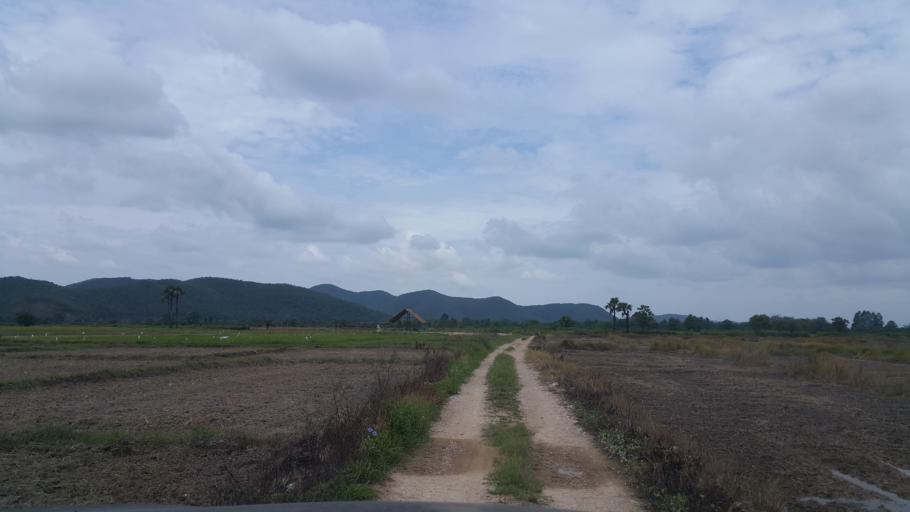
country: TH
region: Lamphun
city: Ban Thi
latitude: 18.6421
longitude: 99.1493
